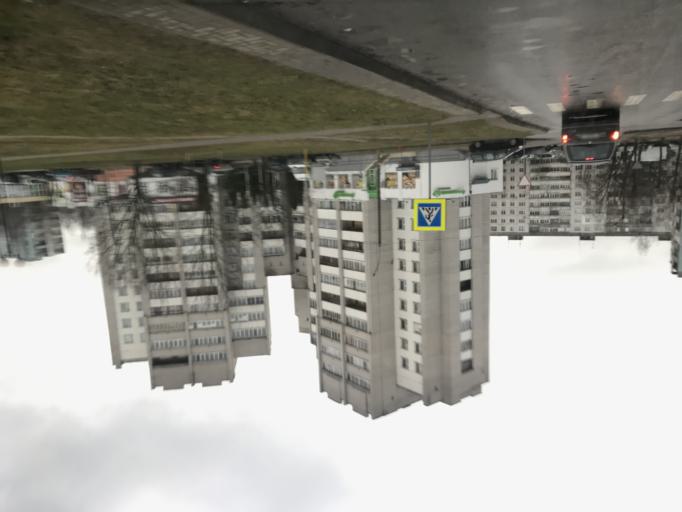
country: BY
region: Mogilev
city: Mahilyow
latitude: 53.8710
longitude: 30.3366
